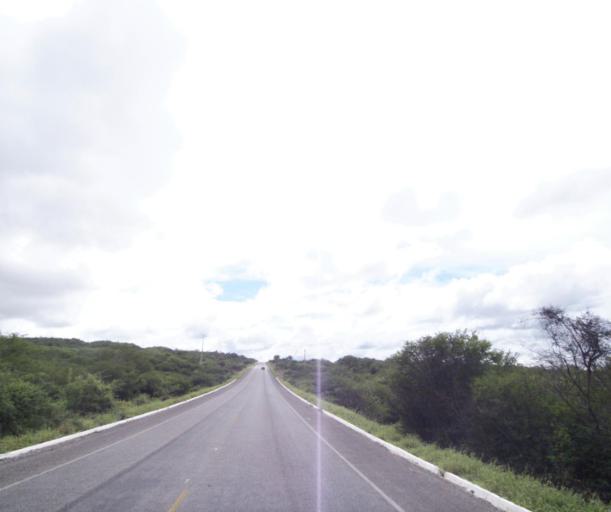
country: BR
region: Bahia
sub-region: Brumado
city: Brumado
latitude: -14.2368
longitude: -41.7068
